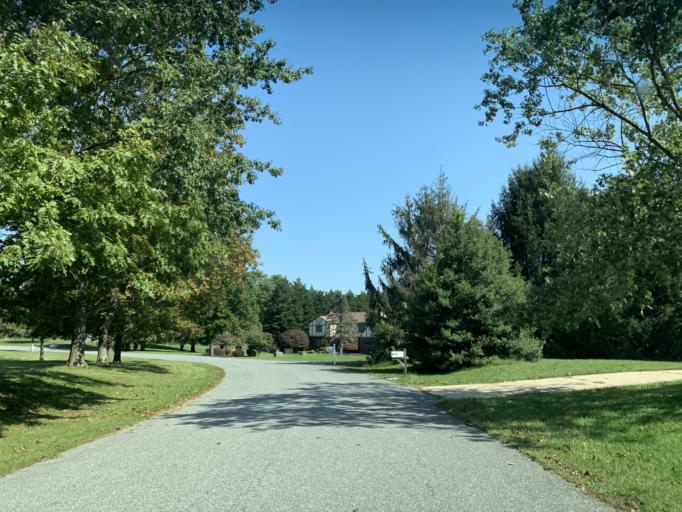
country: US
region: Maryland
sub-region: Harford County
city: Bel Air South
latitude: 39.4855
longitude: -76.3377
